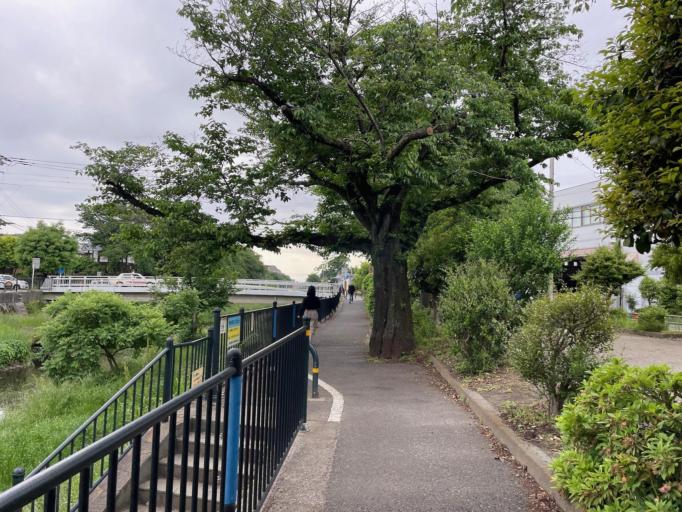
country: JP
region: Tokyo
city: Chofugaoka
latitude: 35.6572
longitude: 139.5556
